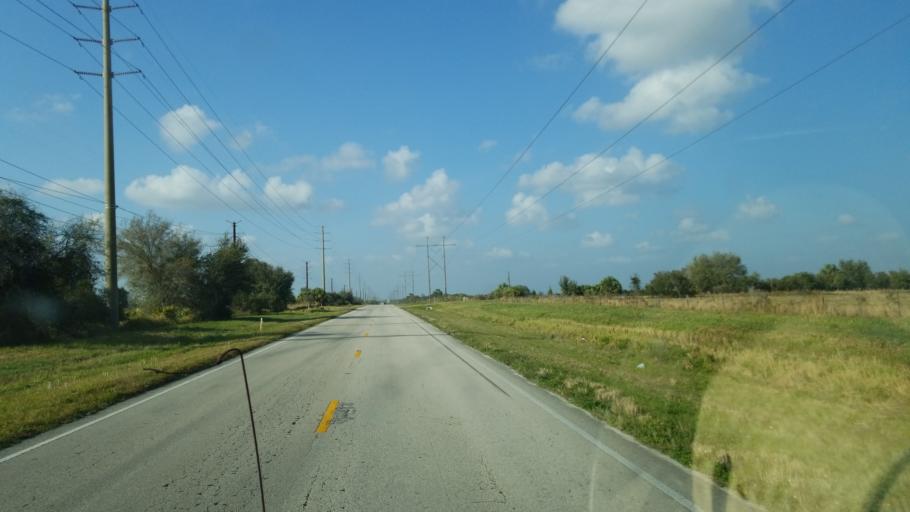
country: US
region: Florida
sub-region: Hardee County
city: Wauchula
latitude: 27.5504
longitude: -81.9316
